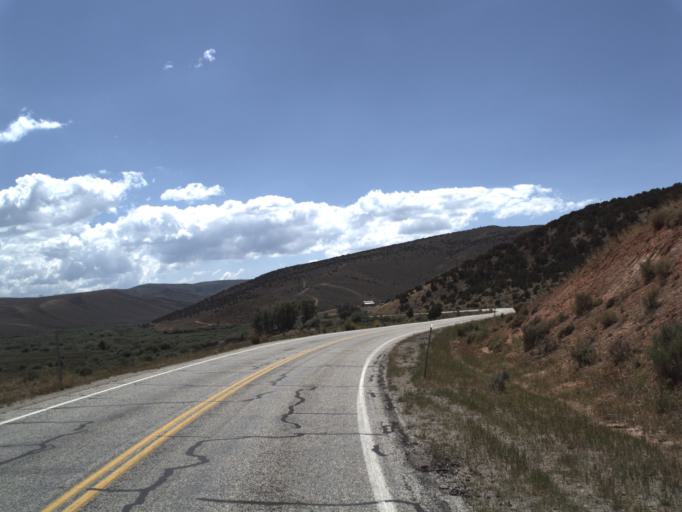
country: US
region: Utah
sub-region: Rich County
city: Randolph
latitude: 41.5019
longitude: -111.2480
